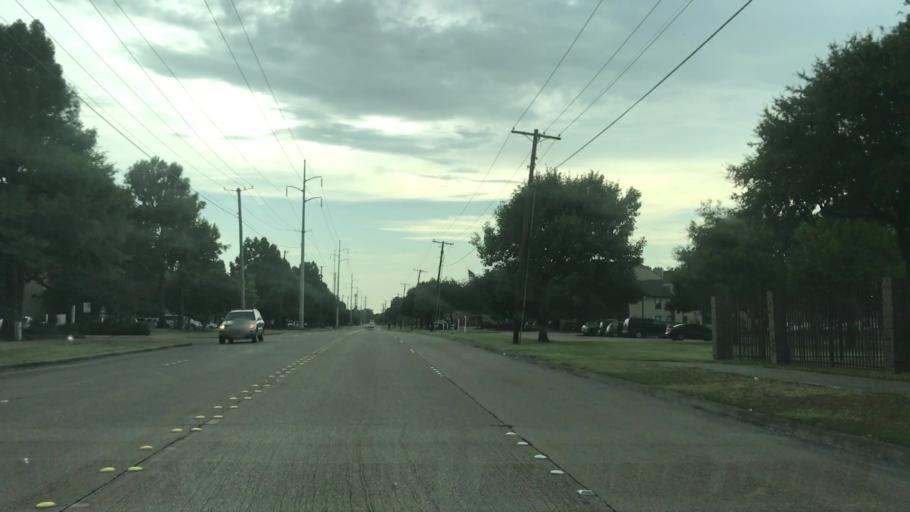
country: US
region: Texas
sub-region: Dallas County
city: Rowlett
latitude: 32.8511
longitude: -96.5745
